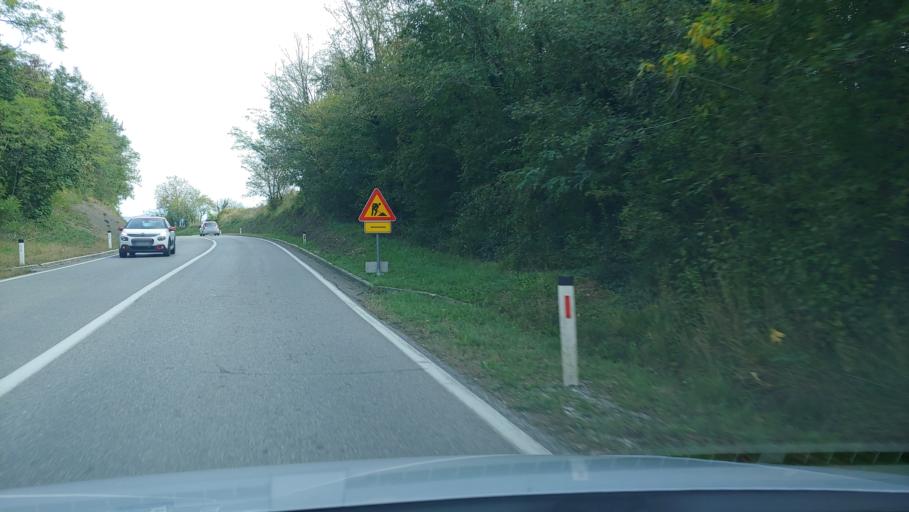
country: SI
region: Ajdovscina
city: Lokavec
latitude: 45.8853
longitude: 13.8354
